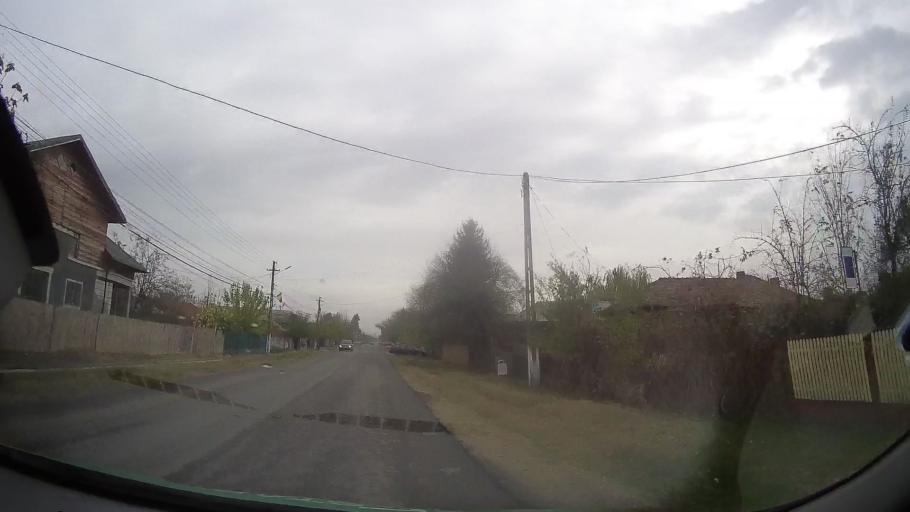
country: RO
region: Prahova
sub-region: Comuna Dumbrava
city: Dumbrava
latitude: 44.8723
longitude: 26.1911
